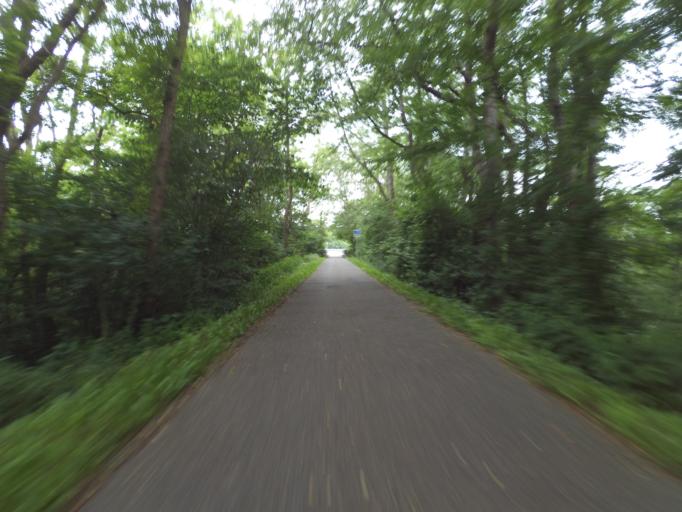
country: DE
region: North Rhine-Westphalia
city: Stolberg
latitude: 50.7398
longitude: 6.1697
